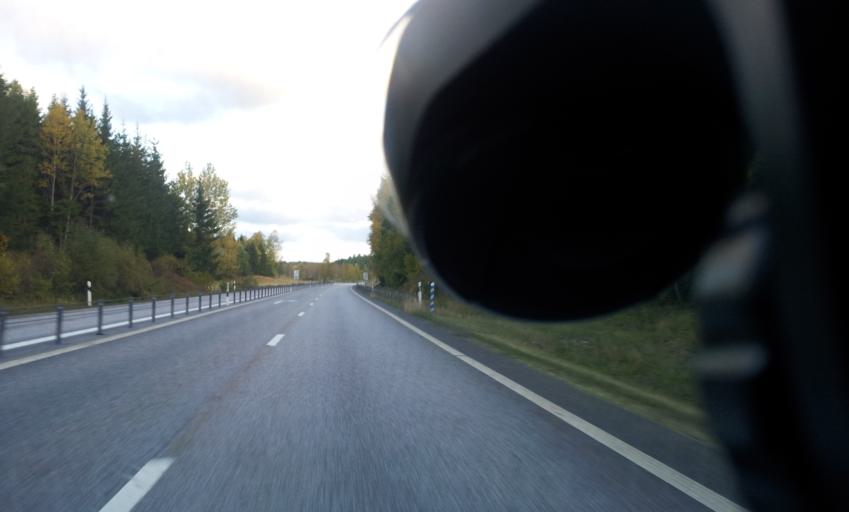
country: SE
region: OEstergoetland
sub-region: Valdemarsviks Kommun
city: Valdemarsvik
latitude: 58.1726
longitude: 16.5373
